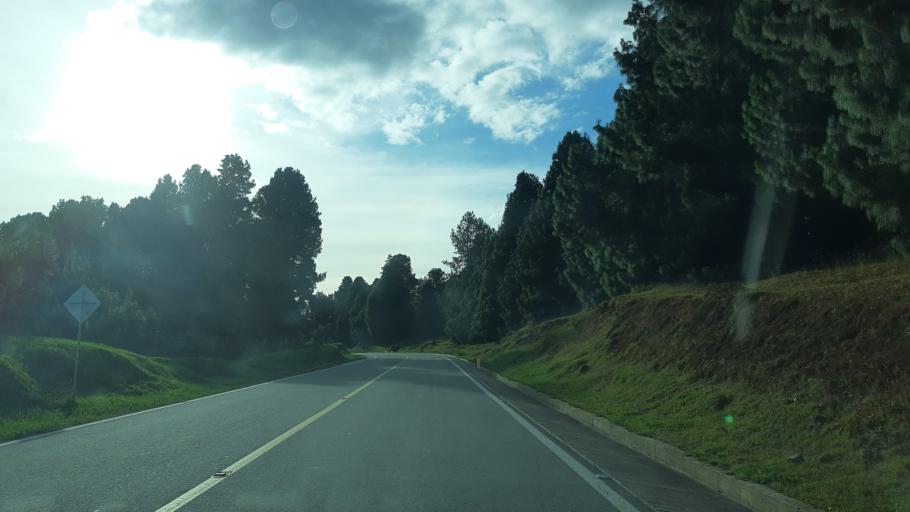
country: CO
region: Cundinamarca
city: Choconta
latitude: 5.0961
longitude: -73.7022
